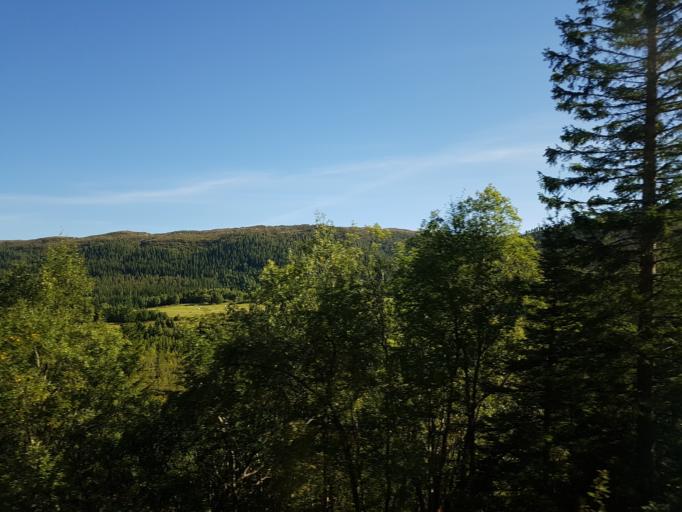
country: NO
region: Sor-Trondelag
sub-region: Afjord
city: A i Afjord
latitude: 63.7816
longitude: 10.2198
